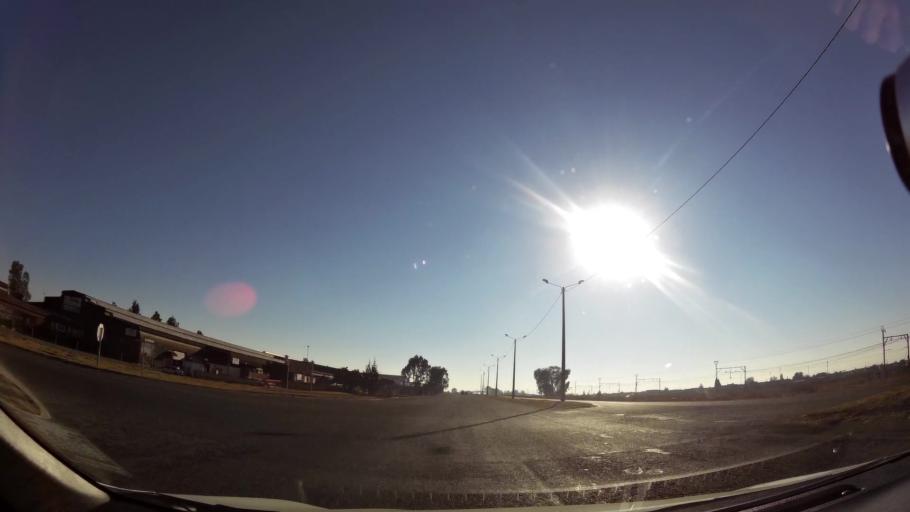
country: ZA
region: Gauteng
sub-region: Ekurhuleni Metropolitan Municipality
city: Germiston
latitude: -26.3556
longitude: 28.1219
